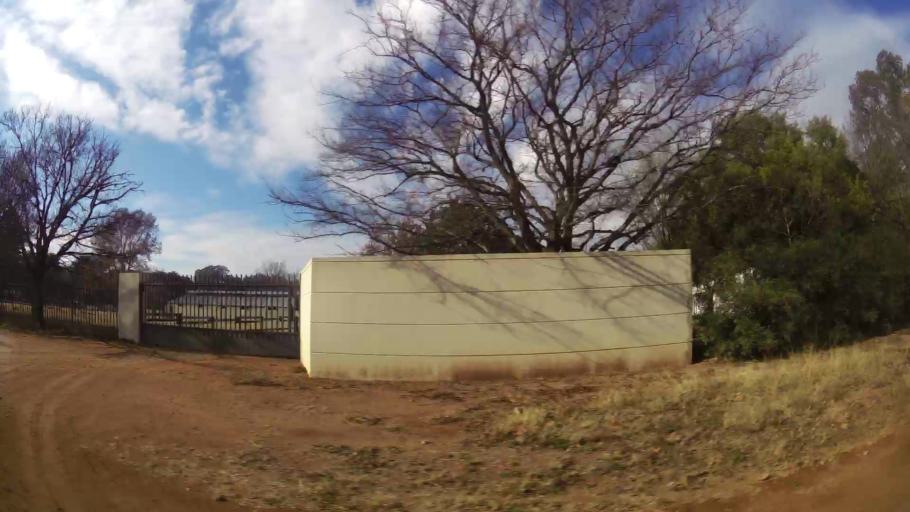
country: ZA
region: Gauteng
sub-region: Sedibeng District Municipality
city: Meyerton
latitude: -26.5491
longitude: 28.0530
